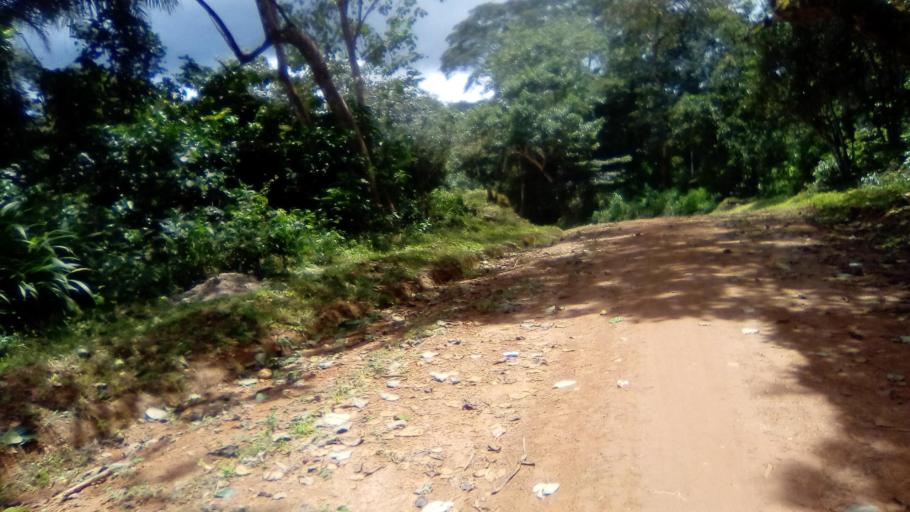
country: SL
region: Eastern Province
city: Giehun
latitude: 8.4985
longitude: -10.9082
